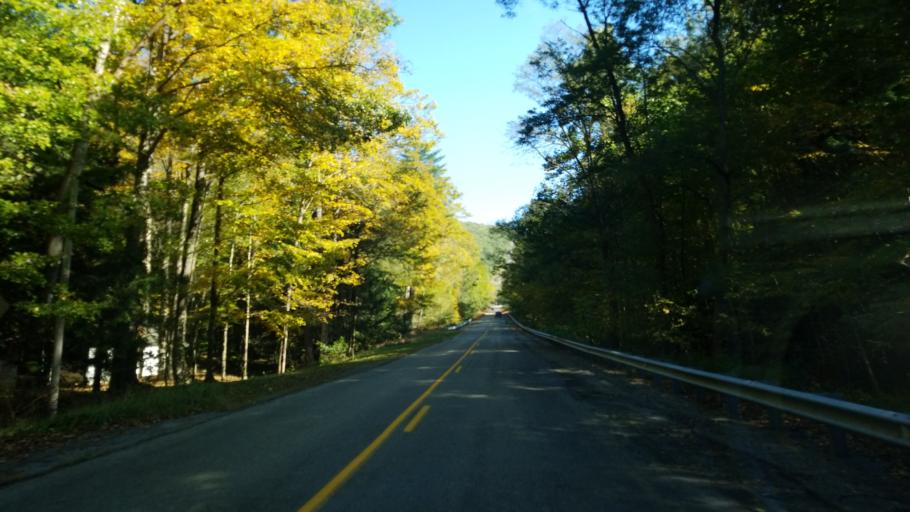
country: US
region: Pennsylvania
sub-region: Elk County
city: Saint Marys
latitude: 41.2658
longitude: -78.4000
